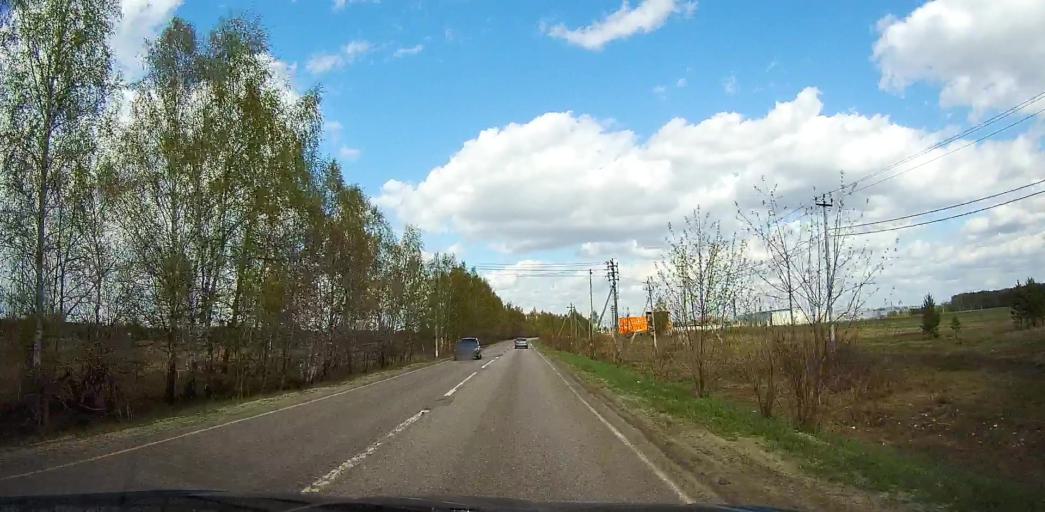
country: RU
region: Moskovskaya
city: Davydovo
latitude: 55.5994
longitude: 38.8410
